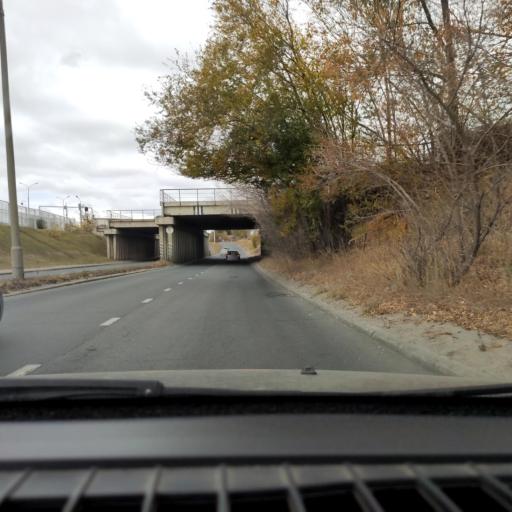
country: RU
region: Samara
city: Tol'yatti
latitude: 53.5669
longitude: 49.2863
